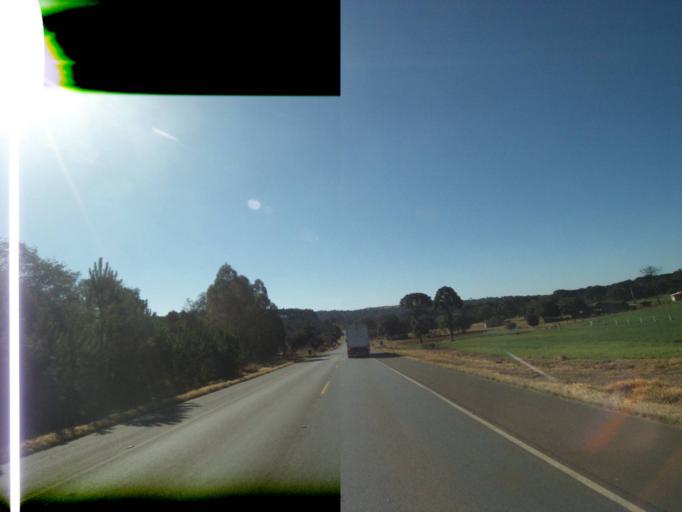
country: BR
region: Parana
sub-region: Tibagi
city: Tibagi
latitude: -24.5928
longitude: -50.4372
